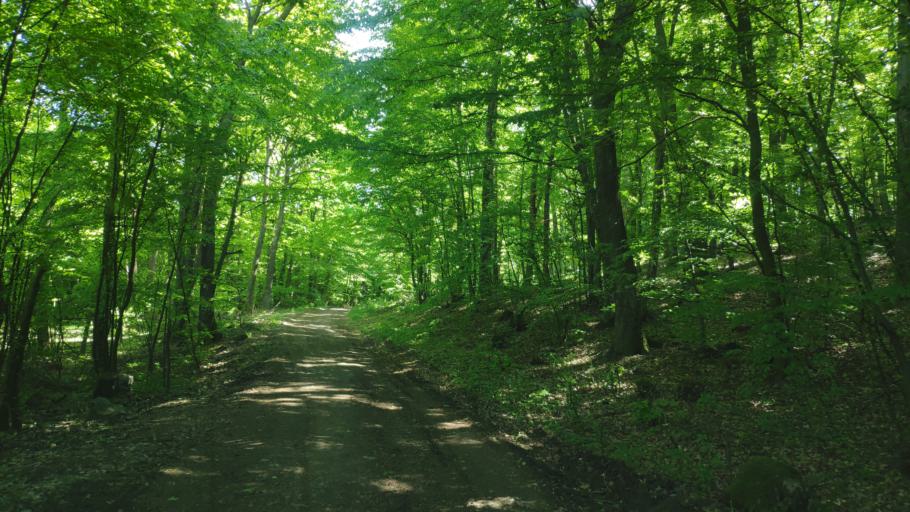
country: SK
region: Kosicky
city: Secovce
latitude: 48.7192
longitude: 21.5807
